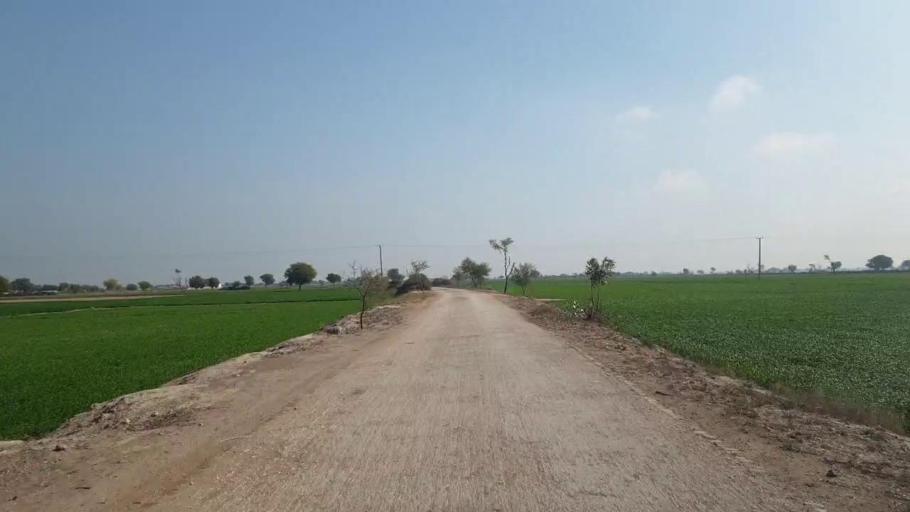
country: PK
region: Sindh
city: Shahdadpur
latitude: 26.0237
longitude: 68.6079
